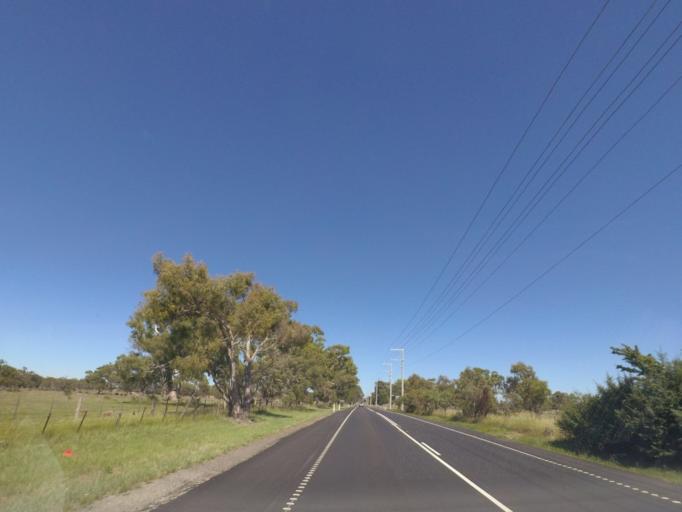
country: AU
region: Victoria
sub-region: Whittlesea
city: Mernda
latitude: -37.5532
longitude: 145.0682
